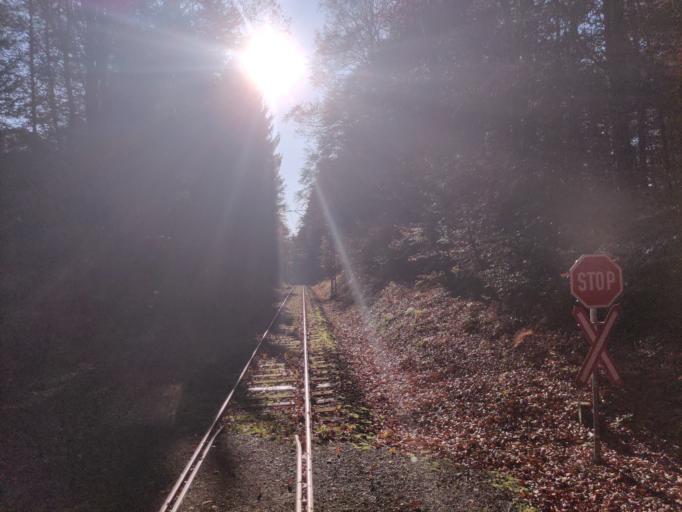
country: AT
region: Styria
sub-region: Politischer Bezirk Suedoststeiermark
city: Maierdorf
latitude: 46.9150
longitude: 15.8409
